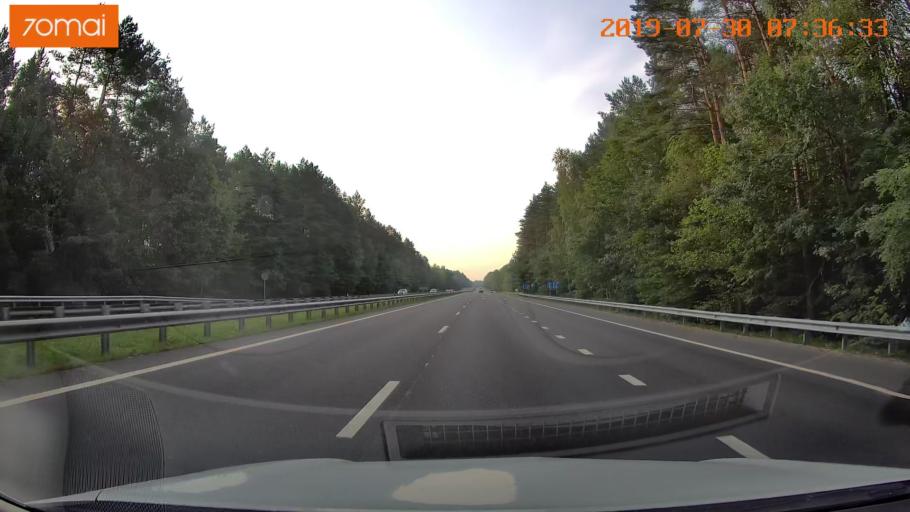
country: RU
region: Kaliningrad
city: Gvardeysk
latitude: 54.6636
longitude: 21.1268
